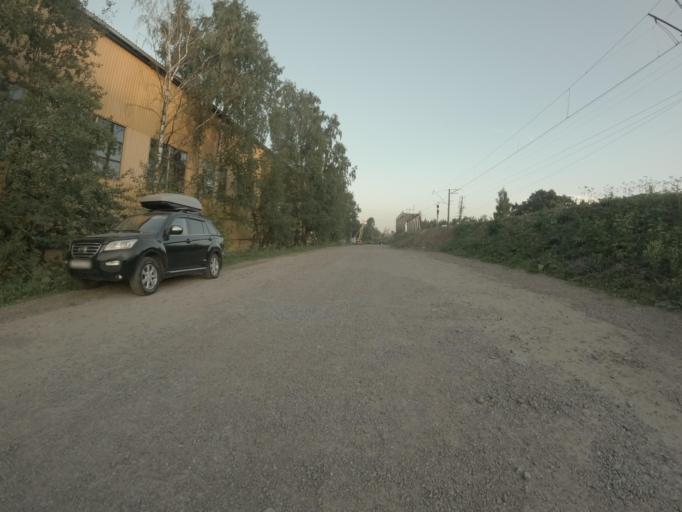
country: RU
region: St.-Petersburg
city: Krasnogvargeisky
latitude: 59.9426
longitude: 30.4481
